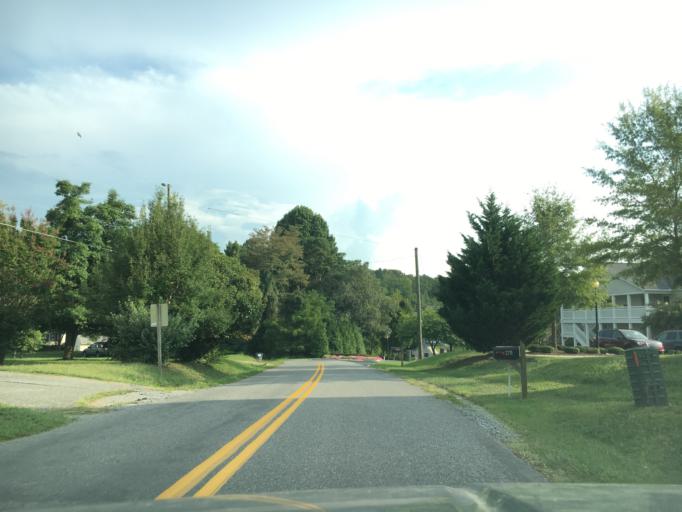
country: US
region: Virginia
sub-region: Campbell County
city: Timberlake
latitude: 37.3385
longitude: -79.2331
